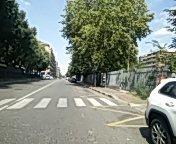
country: IT
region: Piedmont
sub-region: Provincia di Torino
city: Moncalieri
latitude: 45.0299
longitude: 7.6706
